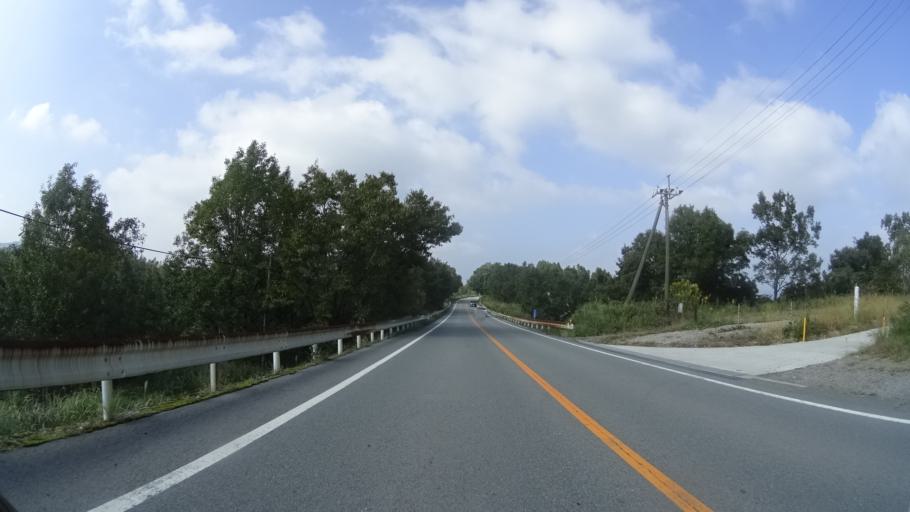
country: JP
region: Kumamoto
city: Aso
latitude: 33.0448
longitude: 131.0682
